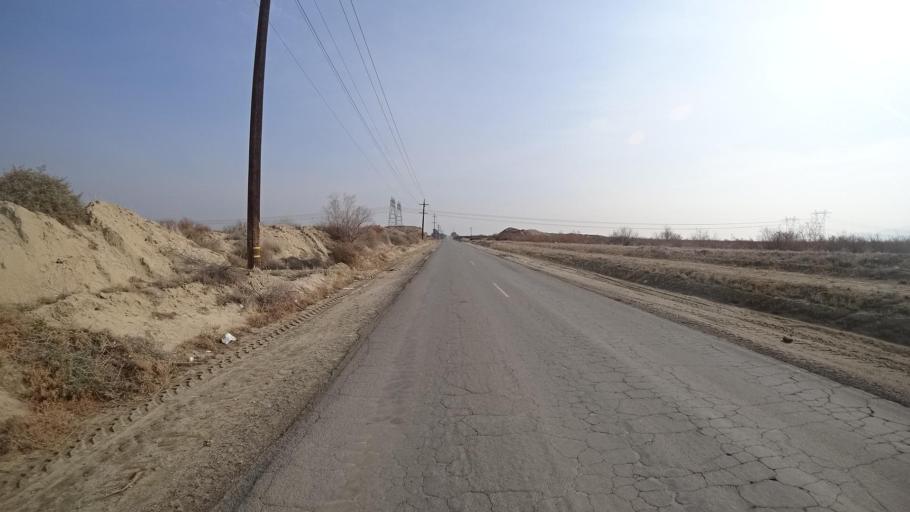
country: US
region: California
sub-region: Kern County
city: Greenfield
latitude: 35.0950
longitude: -119.0502
